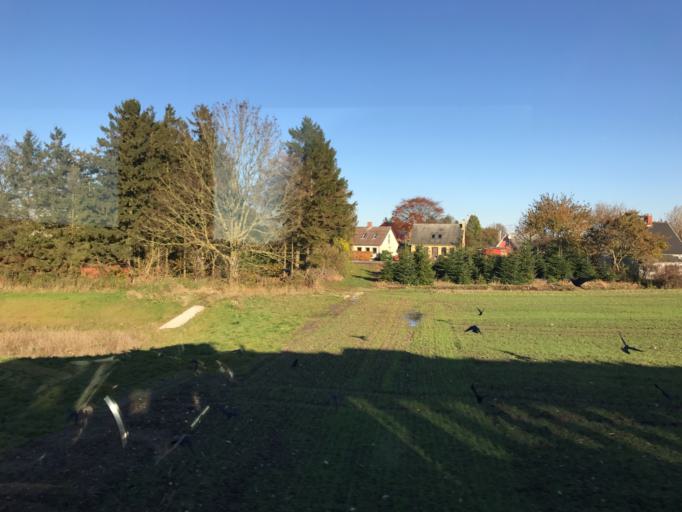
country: DK
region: Zealand
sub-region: Stevns Kommune
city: Store Heddinge
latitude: 55.3193
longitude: 12.3730
